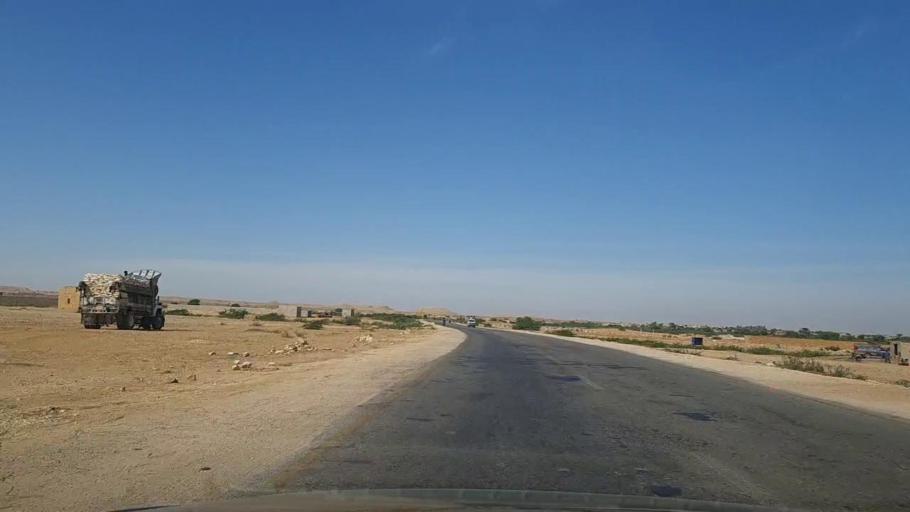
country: PK
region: Sindh
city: Kotri
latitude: 25.1706
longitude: 68.2415
